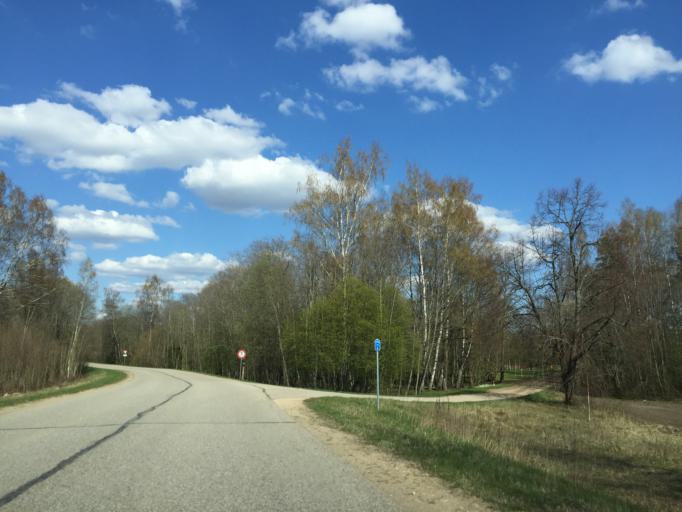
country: LV
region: Seja
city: Loja
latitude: 57.2637
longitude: 24.6035
